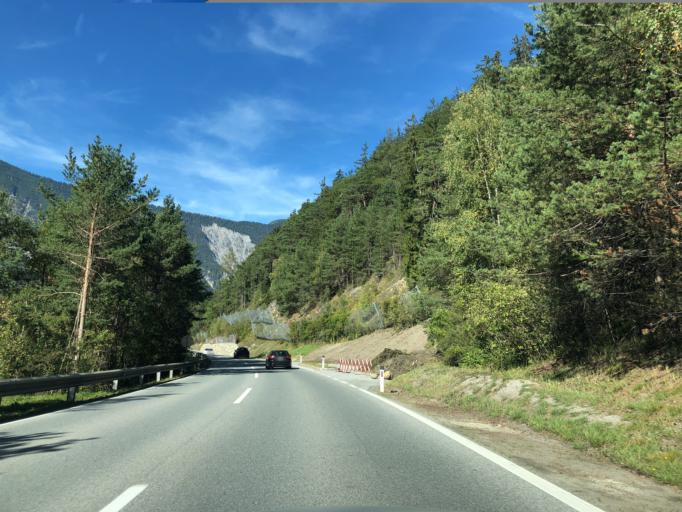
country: AT
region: Tyrol
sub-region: Politischer Bezirk Imst
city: Sautens
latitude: 47.2237
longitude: 10.8614
